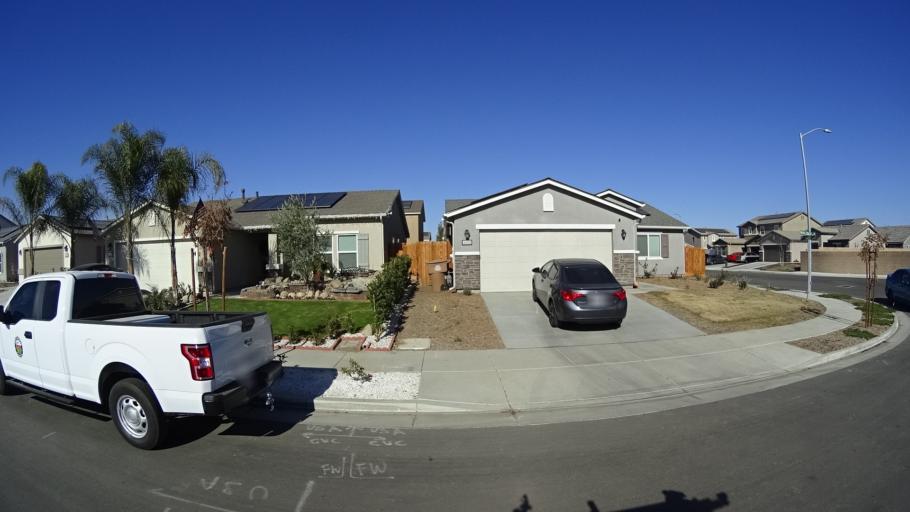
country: US
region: California
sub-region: Kern County
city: Greenfield
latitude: 35.2639
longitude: -119.0696
